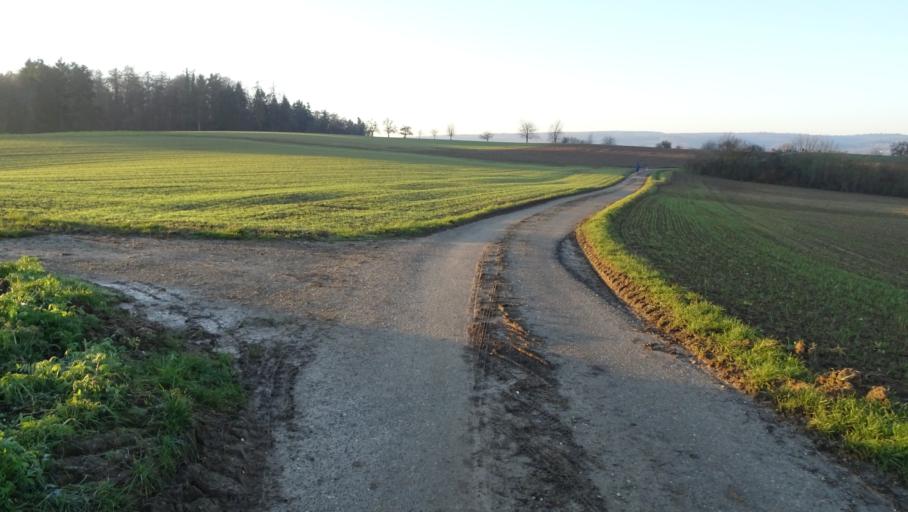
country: DE
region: Baden-Wuerttemberg
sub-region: Karlsruhe Region
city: Aglasterhausen
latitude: 49.3457
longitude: 8.9948
